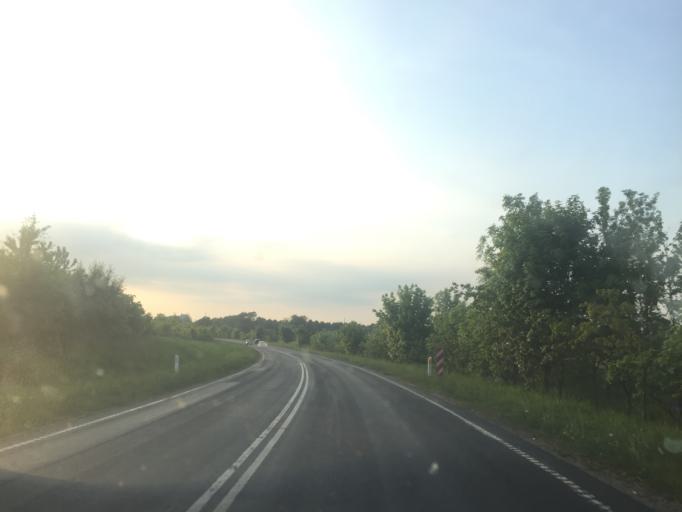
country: DK
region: South Denmark
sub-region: Odense Kommune
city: Neder Holluf
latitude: 55.3476
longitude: 10.4988
